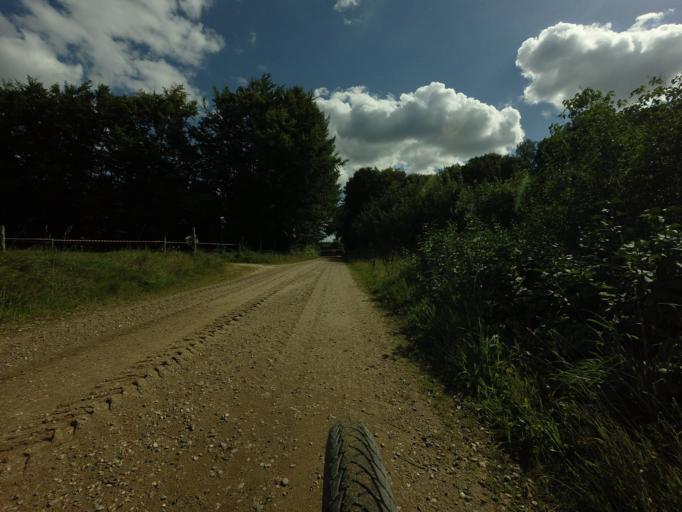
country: DK
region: Central Jutland
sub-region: Ikast-Brande Kommune
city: Brande
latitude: 55.9718
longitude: 9.1548
